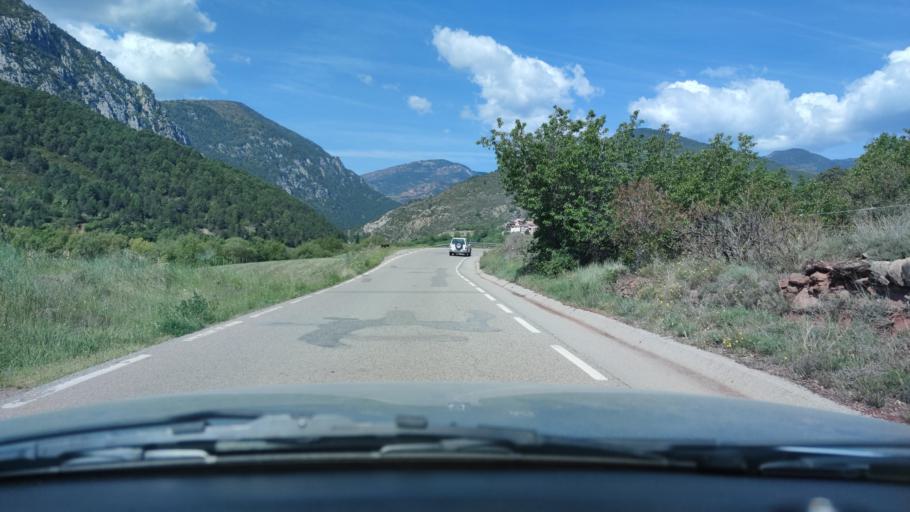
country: ES
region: Catalonia
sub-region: Provincia de Lleida
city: Coll de Nargo
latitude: 42.2911
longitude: 1.3547
